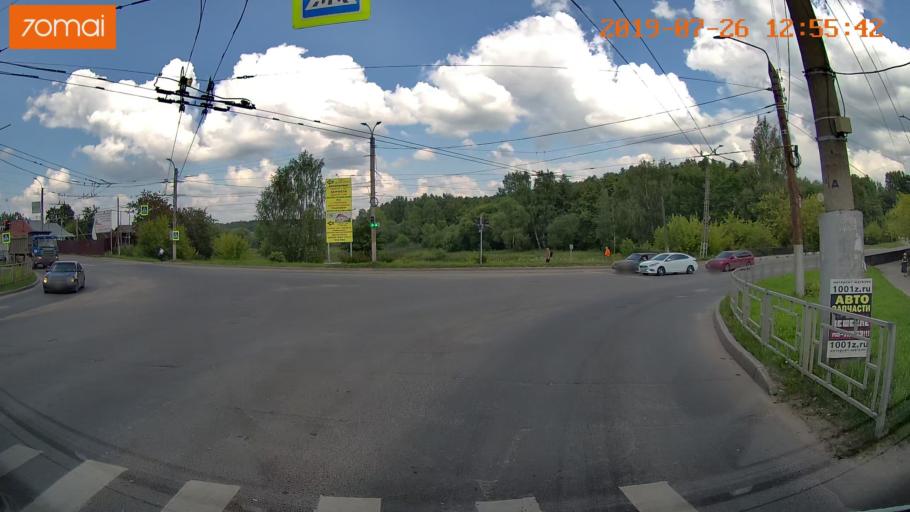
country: RU
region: Ivanovo
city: Bogorodskoye
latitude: 57.0161
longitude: 41.0030
